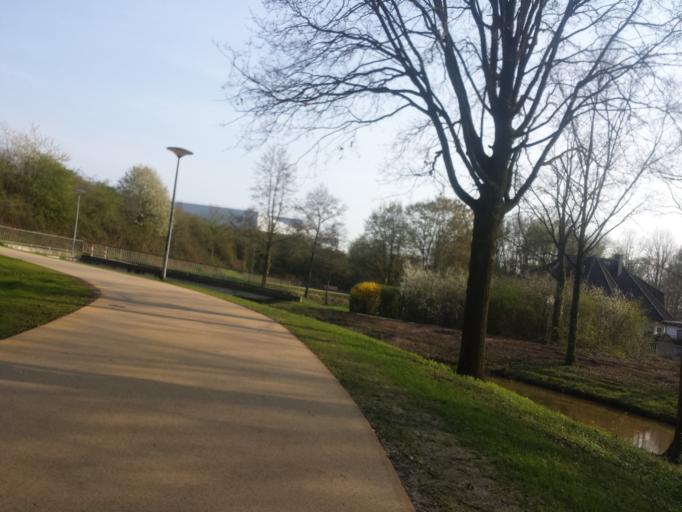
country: DE
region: Lower Saxony
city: Lilienthal
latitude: 53.0672
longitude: 8.9022
